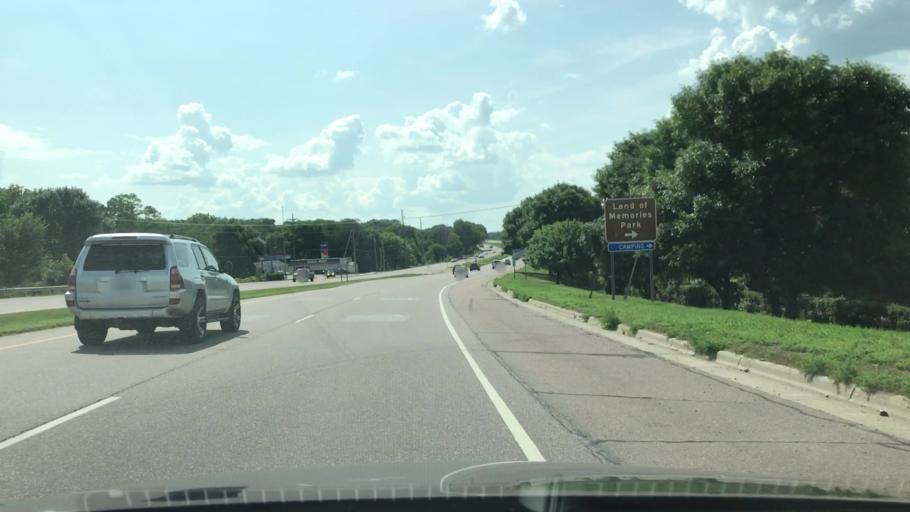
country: US
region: Minnesota
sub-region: Nicollet County
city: North Mankato
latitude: 44.1540
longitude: -94.0351
